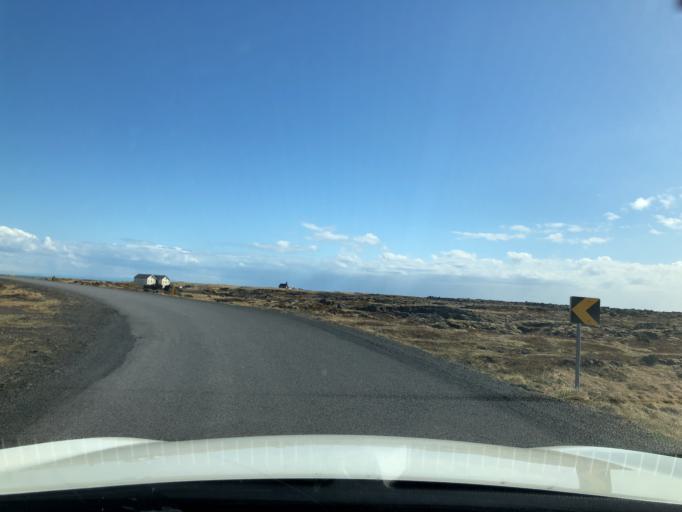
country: IS
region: West
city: Olafsvik
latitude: 64.8253
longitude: -23.3937
